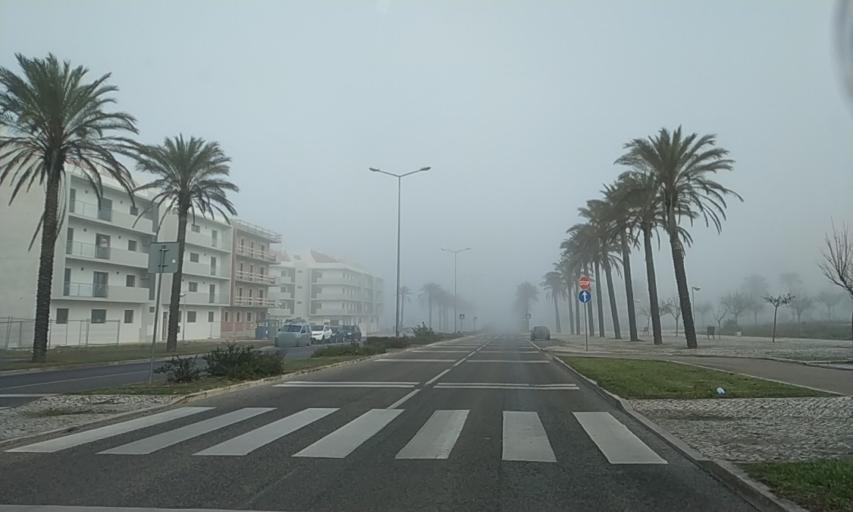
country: PT
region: Setubal
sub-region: Palmela
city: Pinhal Novo
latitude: 38.6203
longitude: -8.9188
